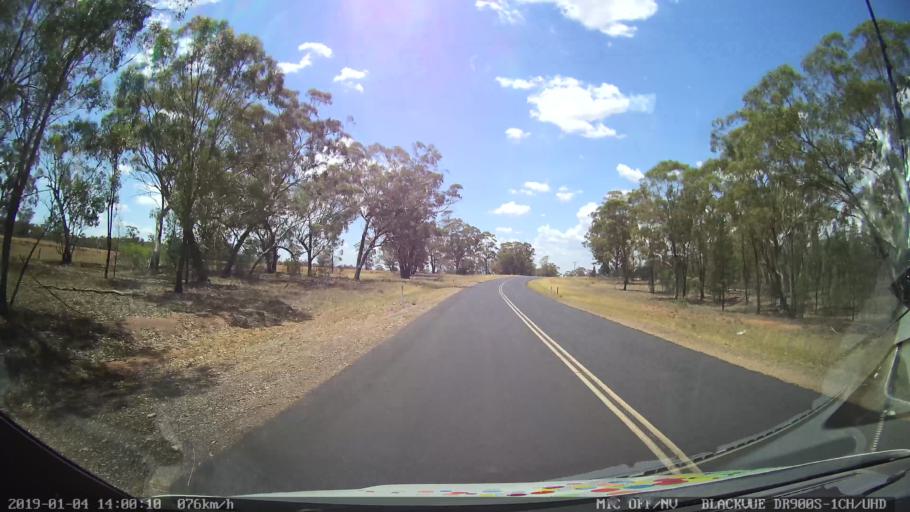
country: AU
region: New South Wales
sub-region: Dubbo Municipality
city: Dubbo
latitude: -32.3089
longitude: 148.5906
